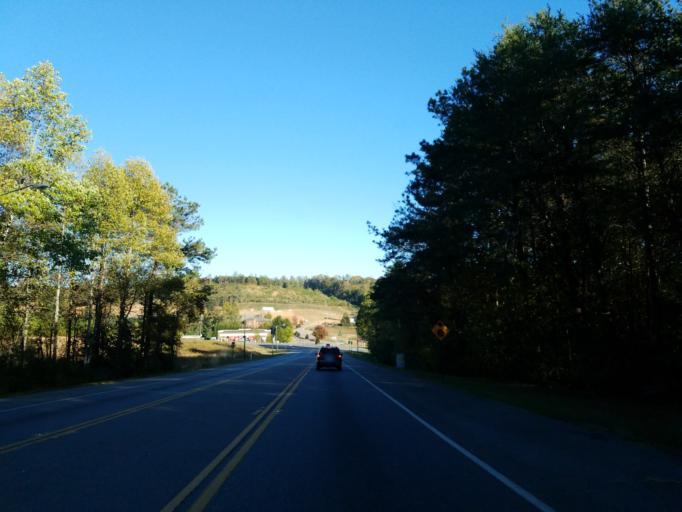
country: US
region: Georgia
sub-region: Cherokee County
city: Ball Ground
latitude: 34.3275
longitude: -84.3921
